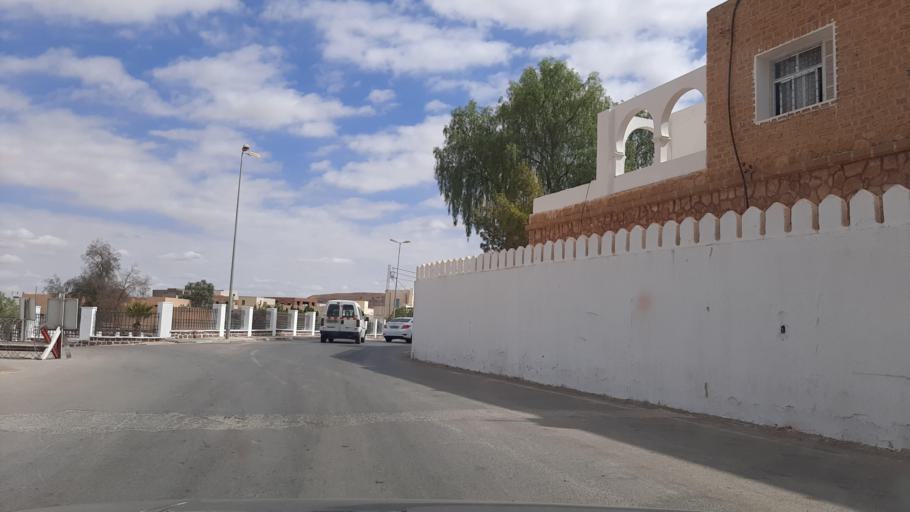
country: TN
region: Tataouine
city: Tataouine
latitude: 32.9263
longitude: 10.4443
